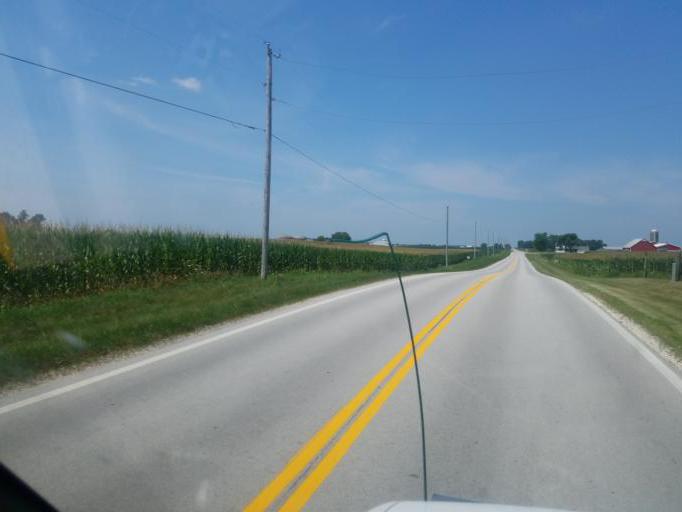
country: US
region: Ohio
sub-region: Auglaize County
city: New Bremen
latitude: 40.4168
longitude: -84.4337
